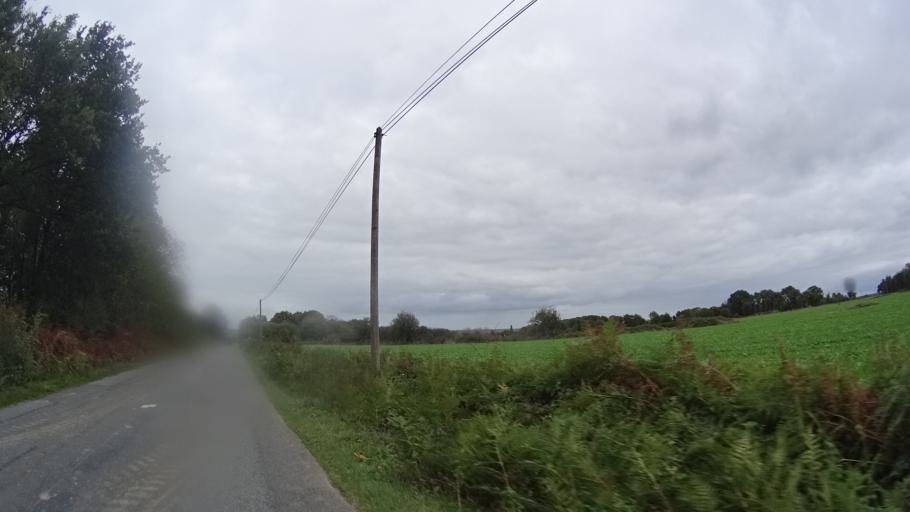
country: FR
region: Brittany
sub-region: Departement d'Ille-et-Vilaine
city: Paimpont
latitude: 48.0886
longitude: -2.1292
